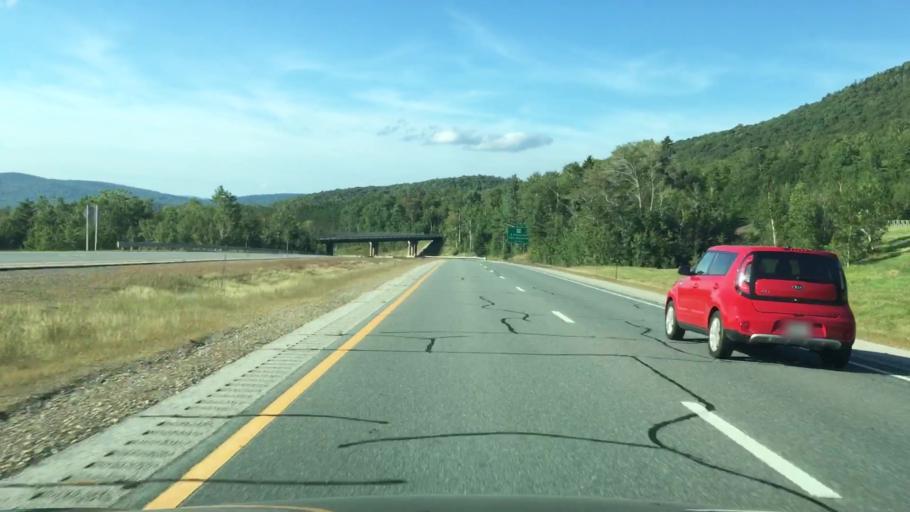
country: US
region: New Hampshire
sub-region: Grafton County
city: Deerfield
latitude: 44.1961
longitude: -71.6813
